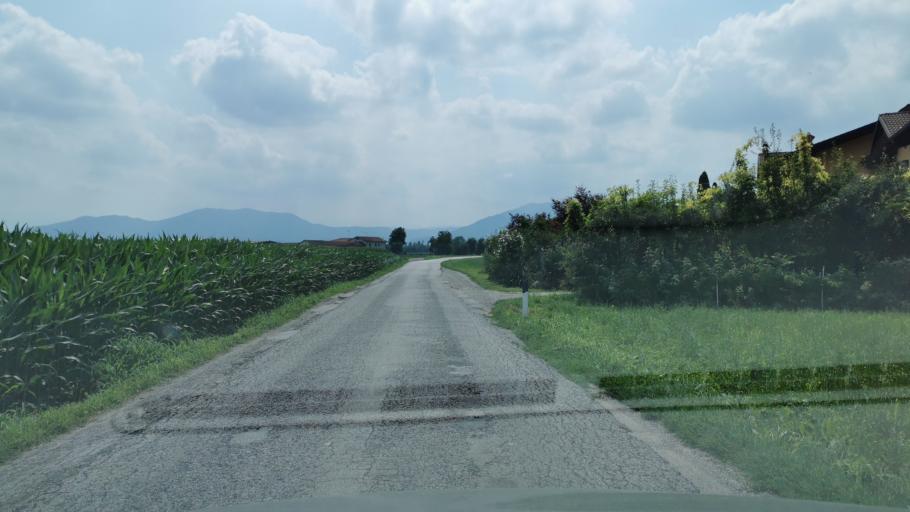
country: IT
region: Piedmont
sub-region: Provincia di Cuneo
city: Roata Rossi
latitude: 44.4324
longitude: 7.4905
